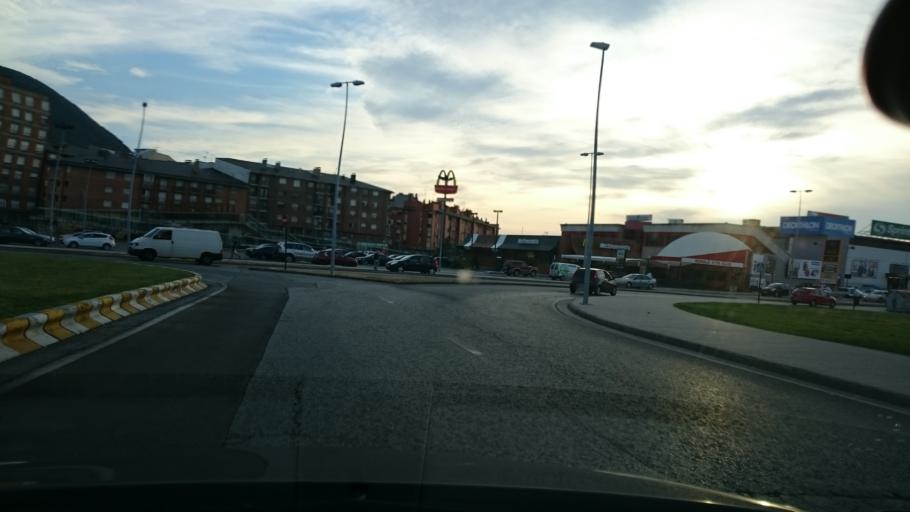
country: ES
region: Castille and Leon
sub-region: Provincia de Leon
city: Ponferrada
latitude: 42.5491
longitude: -6.6058
